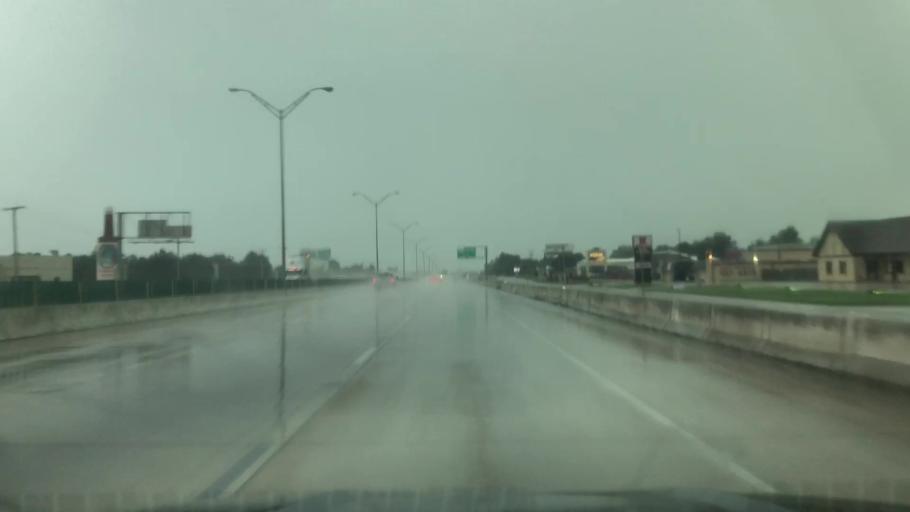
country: US
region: Oklahoma
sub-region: Rogers County
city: Catoosa
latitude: 36.1553
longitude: -95.8377
